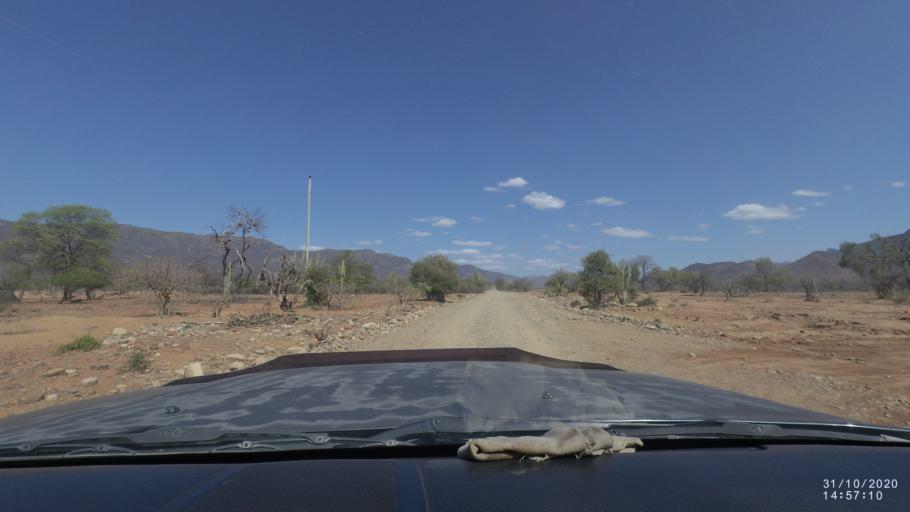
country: BO
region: Cochabamba
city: Aiquile
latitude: -18.2421
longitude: -64.8452
